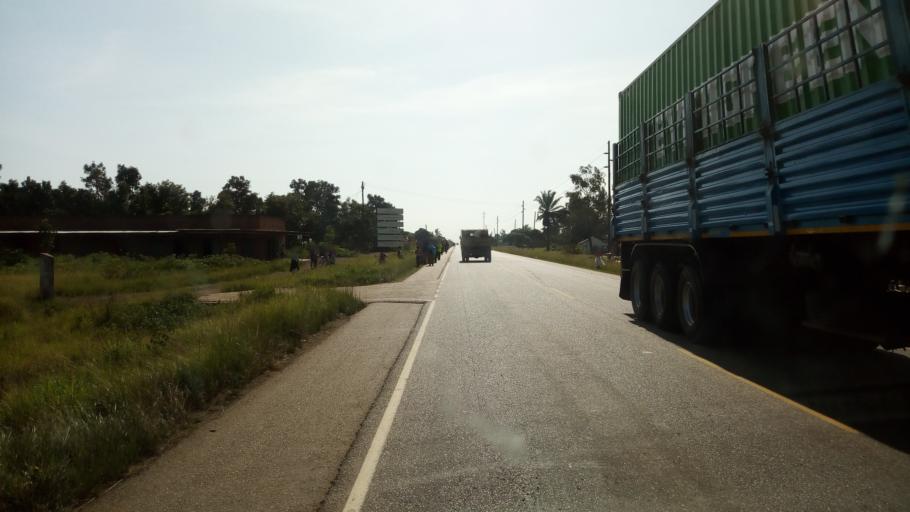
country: UG
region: Eastern Region
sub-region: Bugiri District
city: Bugiri
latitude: 0.5321
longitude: 33.8745
